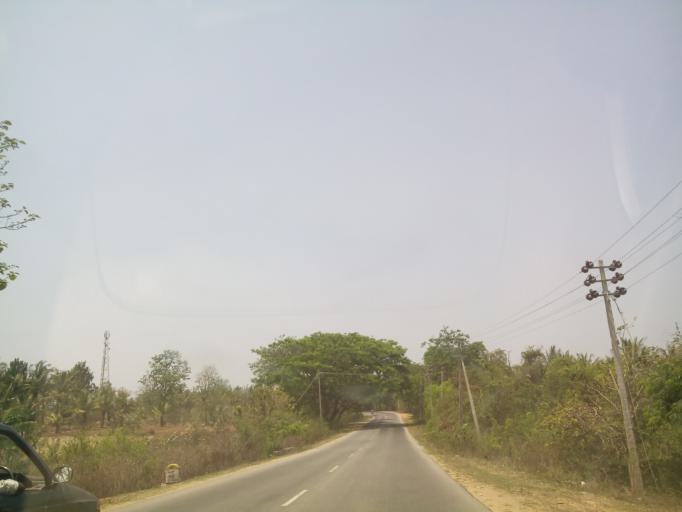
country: IN
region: Karnataka
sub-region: Hassan
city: Alur
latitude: 12.9825
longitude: 76.0304
